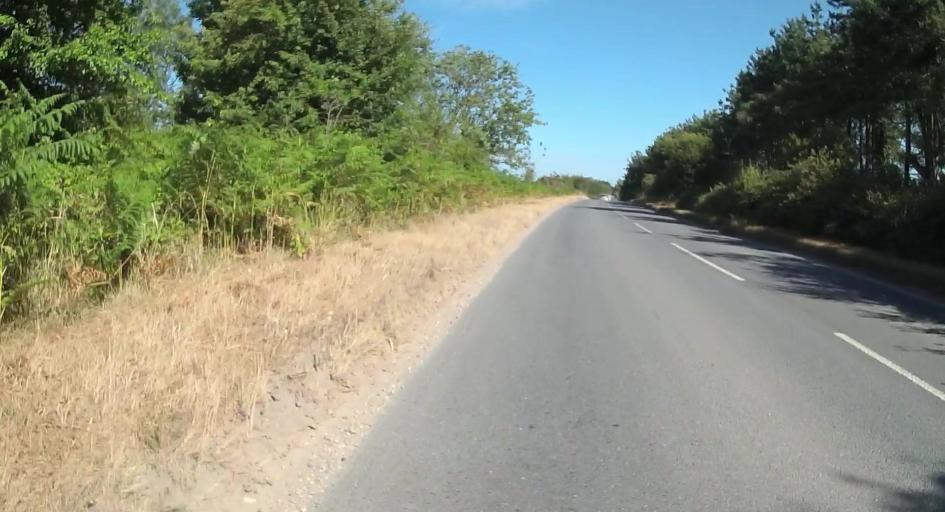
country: GB
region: England
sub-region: Dorset
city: Wool
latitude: 50.6989
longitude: -2.1898
